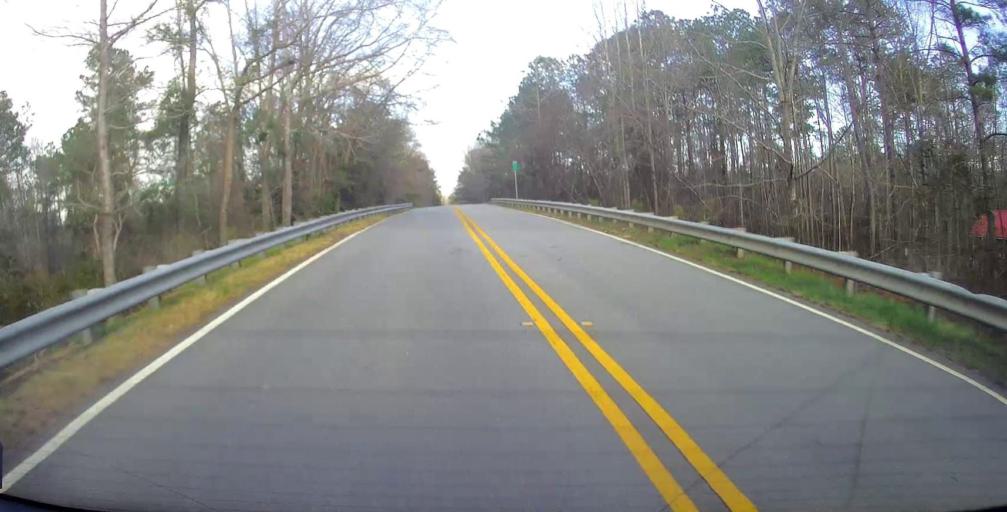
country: US
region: Georgia
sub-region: Harris County
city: Hamilton
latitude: 32.6247
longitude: -84.8121
